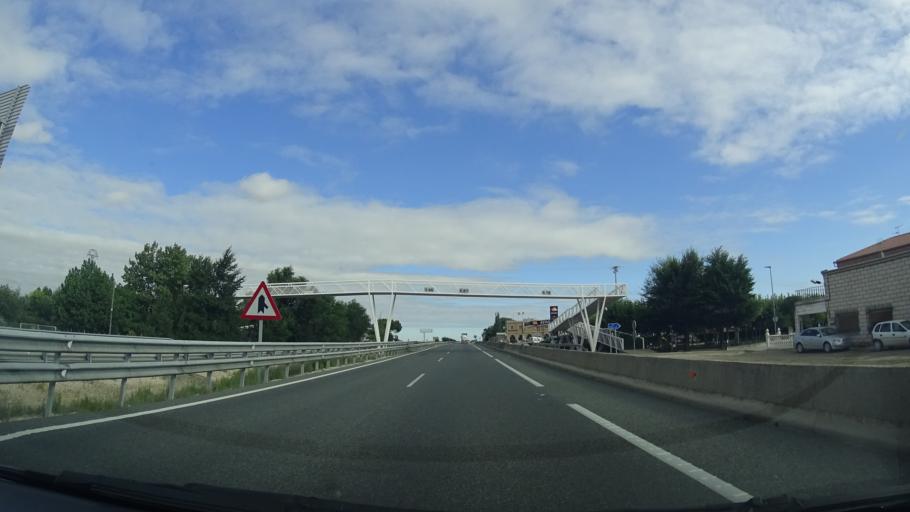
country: ES
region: Castille and Leon
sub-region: Provincia de Valladolid
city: Ataquines
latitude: 41.1803
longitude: -4.8072
